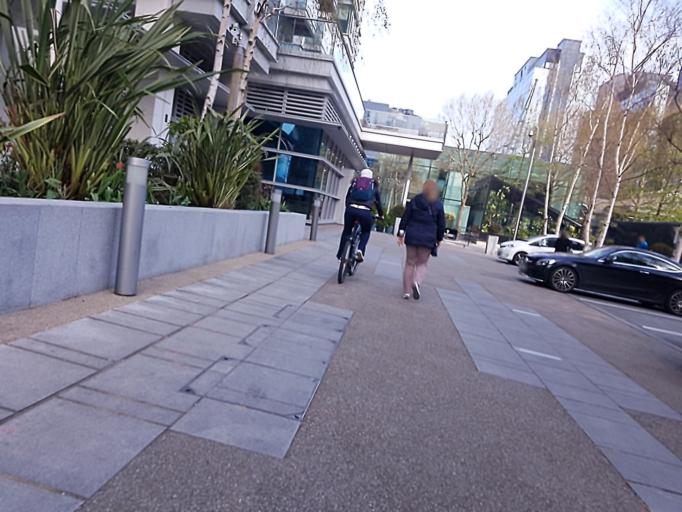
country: GB
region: England
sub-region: Greater London
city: Poplar
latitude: 51.4997
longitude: -0.0181
